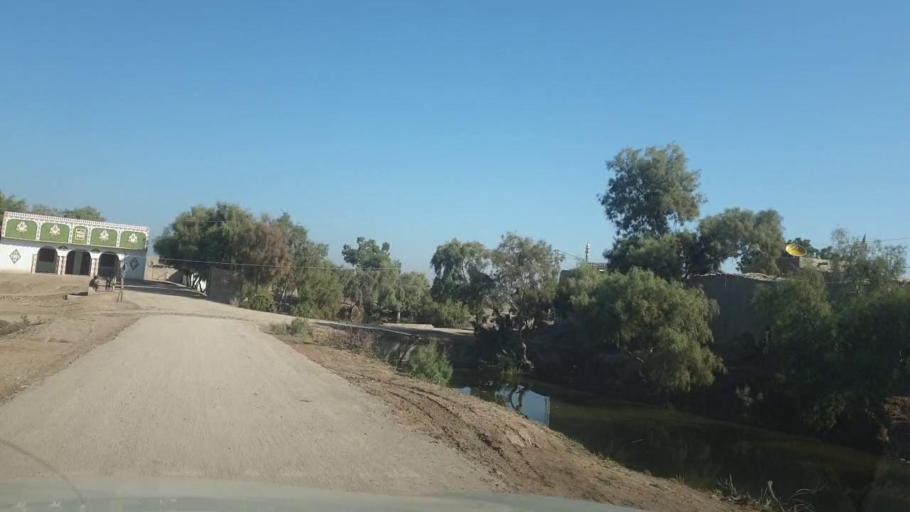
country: PK
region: Sindh
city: Bhan
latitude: 26.5445
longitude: 67.6602
